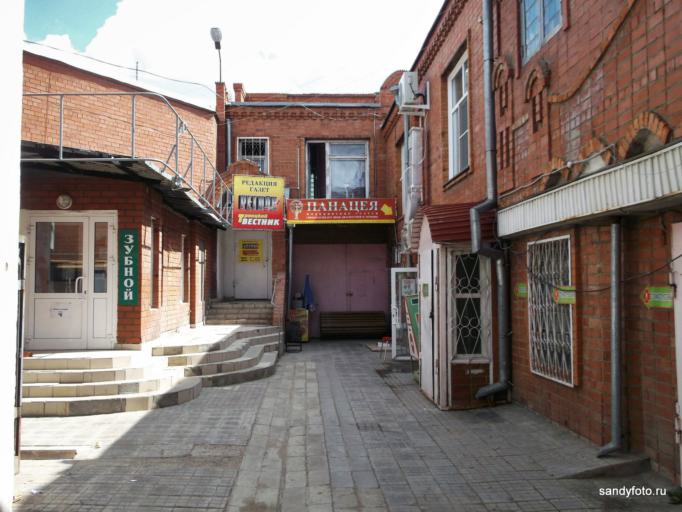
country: RU
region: Chelyabinsk
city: Troitsk
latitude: 54.0866
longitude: 61.5528
